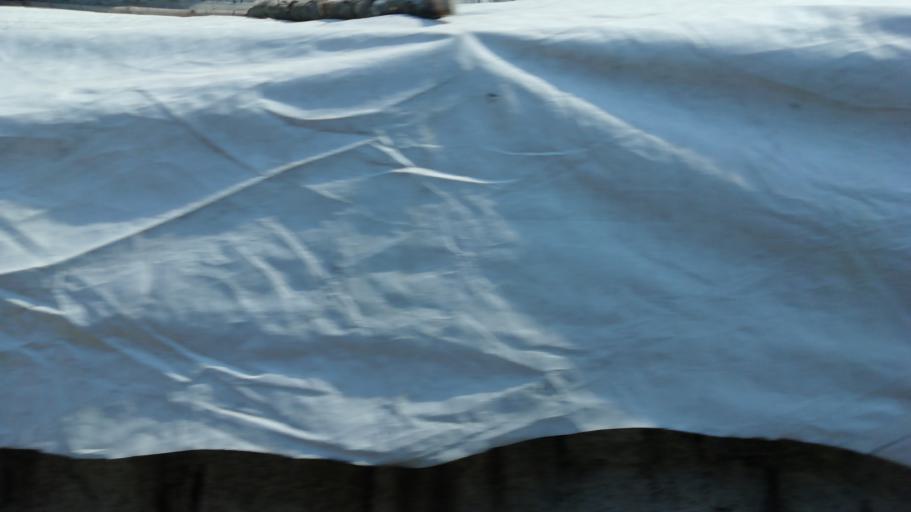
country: TR
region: Karabuk
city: Karabuk
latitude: 41.1164
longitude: 32.5749
